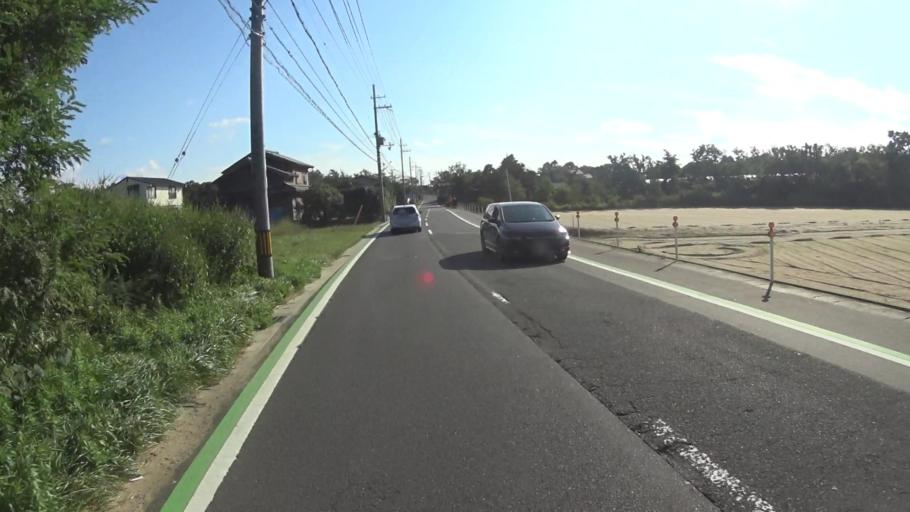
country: JP
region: Hyogo
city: Toyooka
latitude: 35.6536
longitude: 134.9530
